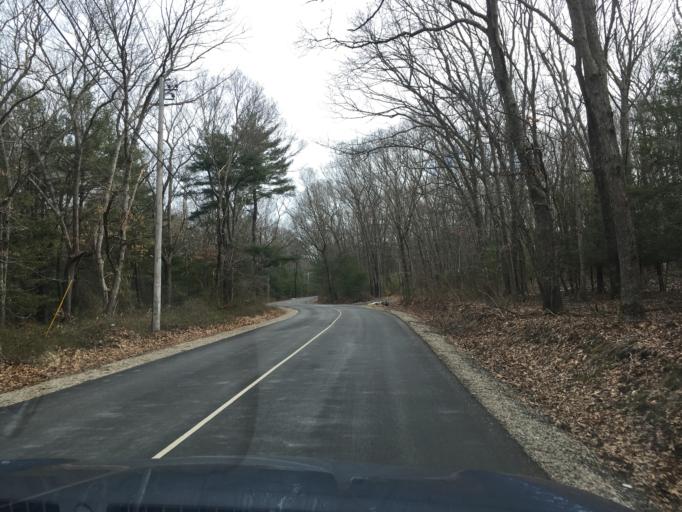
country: US
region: Rhode Island
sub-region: Kent County
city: East Greenwich
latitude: 41.6452
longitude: -71.4377
